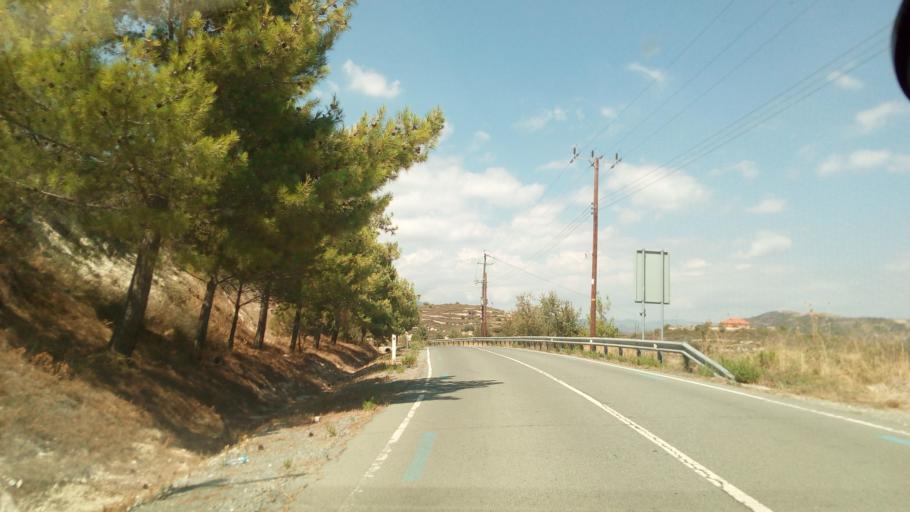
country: CY
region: Limassol
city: Pachna
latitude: 34.8255
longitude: 32.8405
